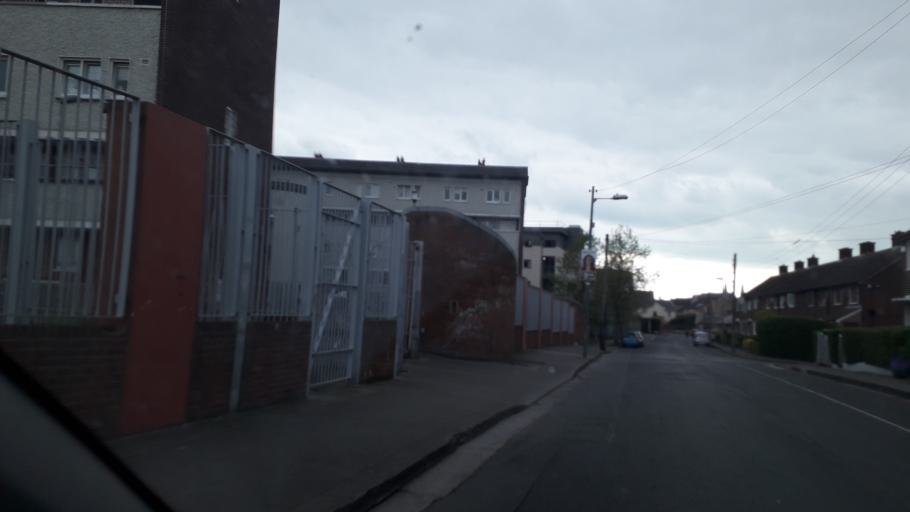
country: IE
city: Greenhills
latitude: 53.3386
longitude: -6.3185
